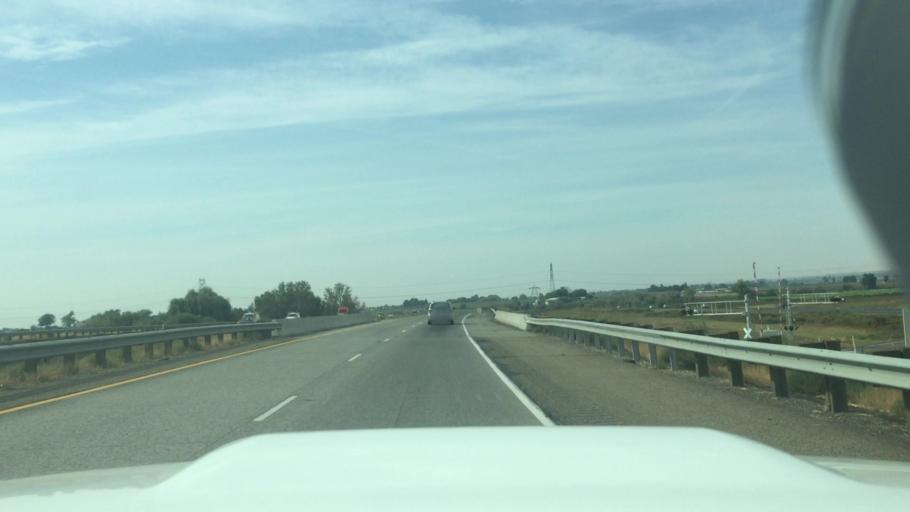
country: US
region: Washington
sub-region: Yakima County
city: Granger
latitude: 46.3336
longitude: -120.1248
